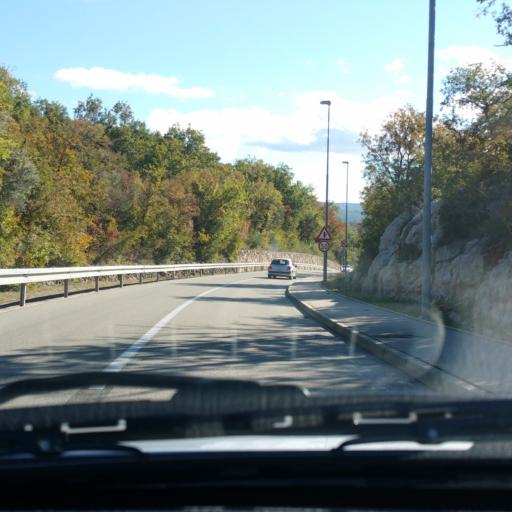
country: HR
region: Primorsko-Goranska
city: Omisalj
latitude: 45.2071
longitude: 14.5600
